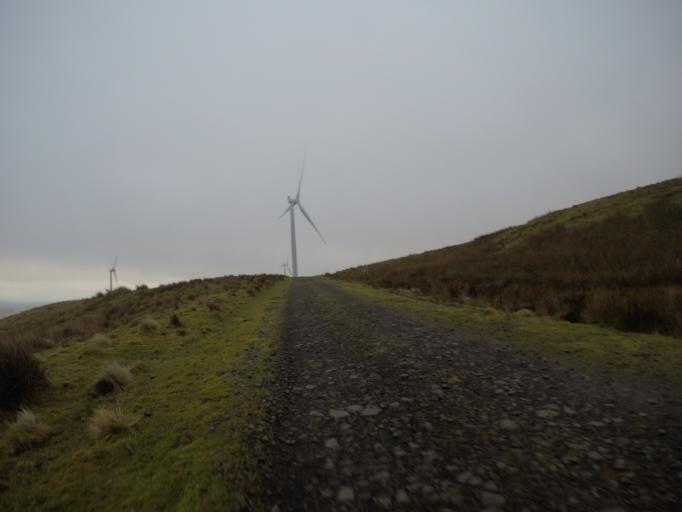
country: GB
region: Scotland
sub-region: North Ayrshire
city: Dalry
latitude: 55.7384
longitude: -4.7781
